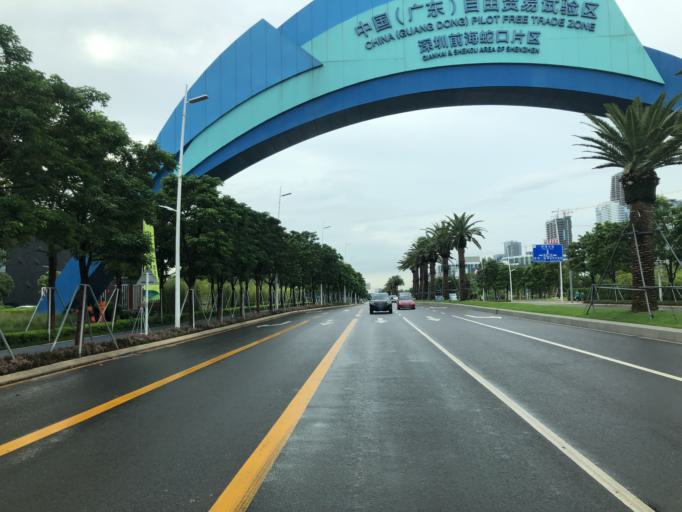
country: CN
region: Guangdong
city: Nantou
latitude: 22.5208
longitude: 113.8987
